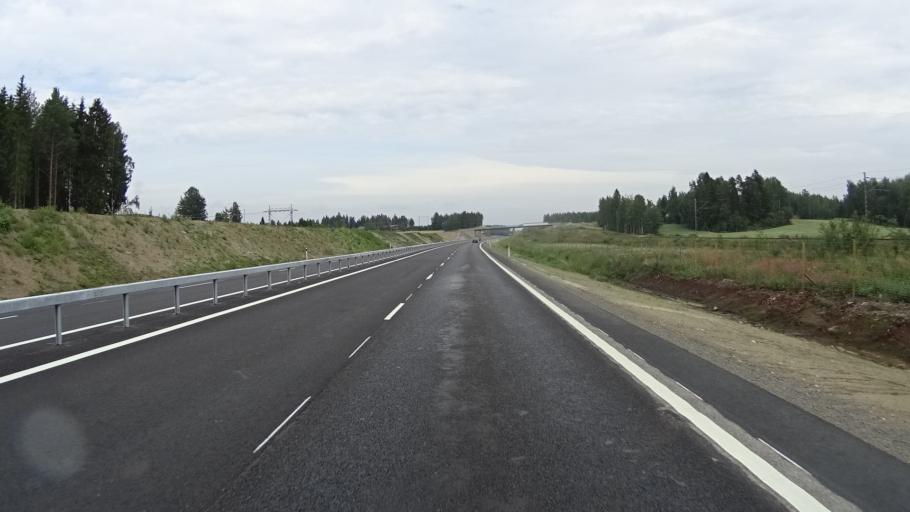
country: FI
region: South Karelia
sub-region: Lappeenranta
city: Lemi
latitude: 60.9601
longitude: 27.8384
